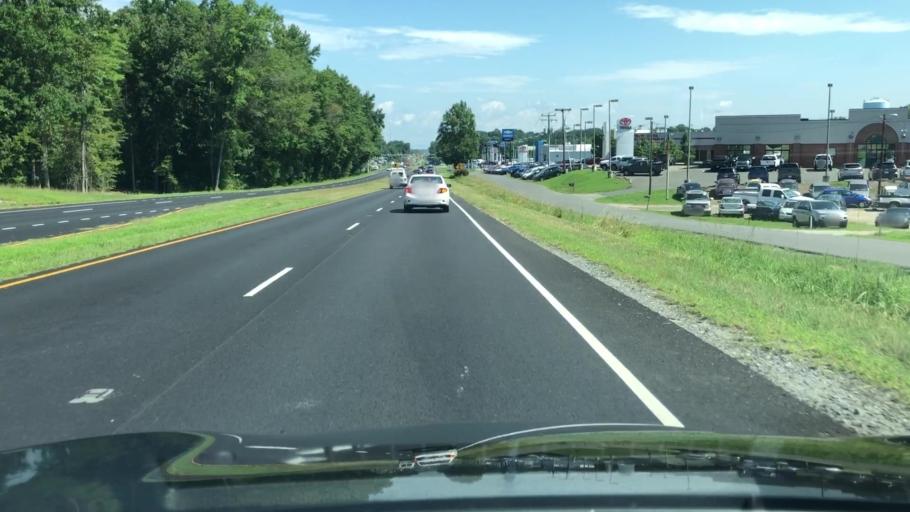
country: US
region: Virginia
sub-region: City of Fredericksburg
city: Fredericksburg
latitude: 38.2685
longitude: -77.4938
